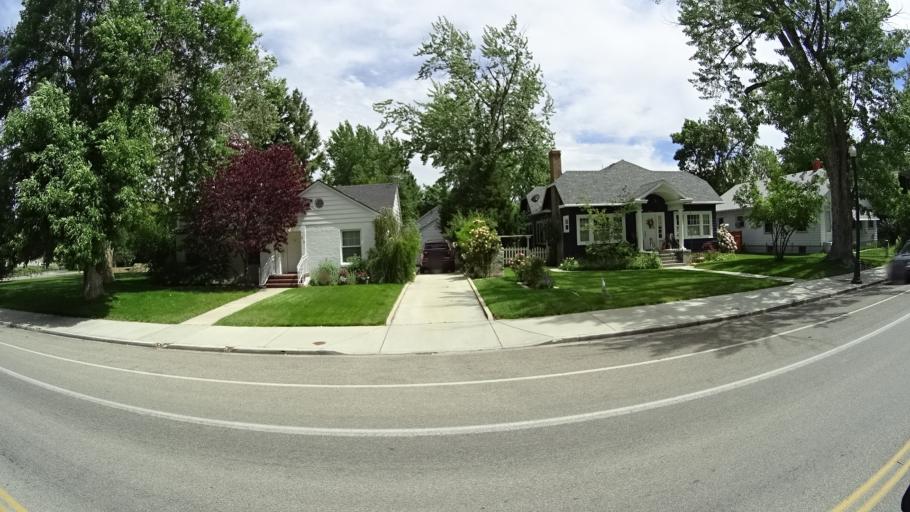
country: US
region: Idaho
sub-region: Ada County
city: Boise
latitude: 43.6085
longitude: -116.1860
